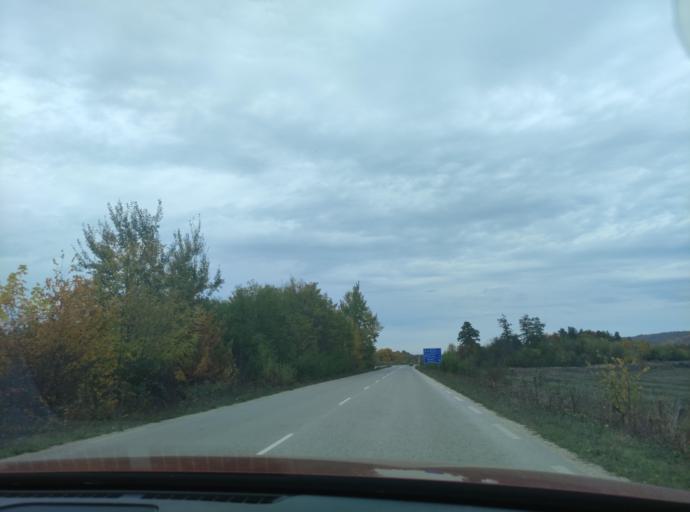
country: BG
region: Montana
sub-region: Obshtina Berkovitsa
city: Berkovitsa
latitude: 43.2413
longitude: 23.1633
